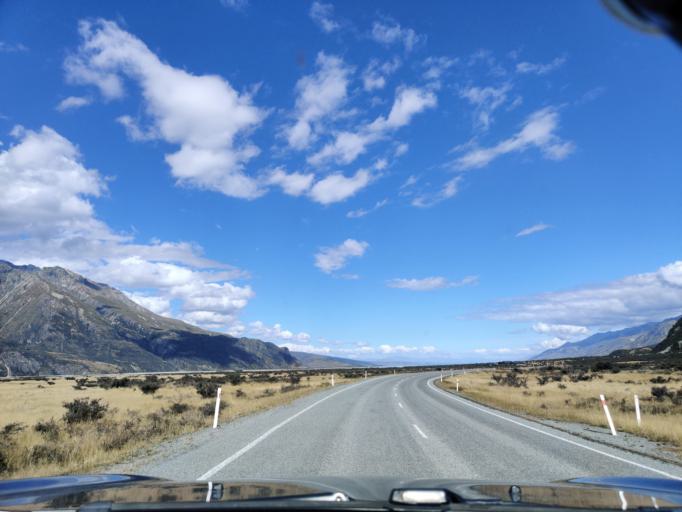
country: NZ
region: Canterbury
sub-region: Timaru District
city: Pleasant Point
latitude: -43.7507
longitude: 170.1178
